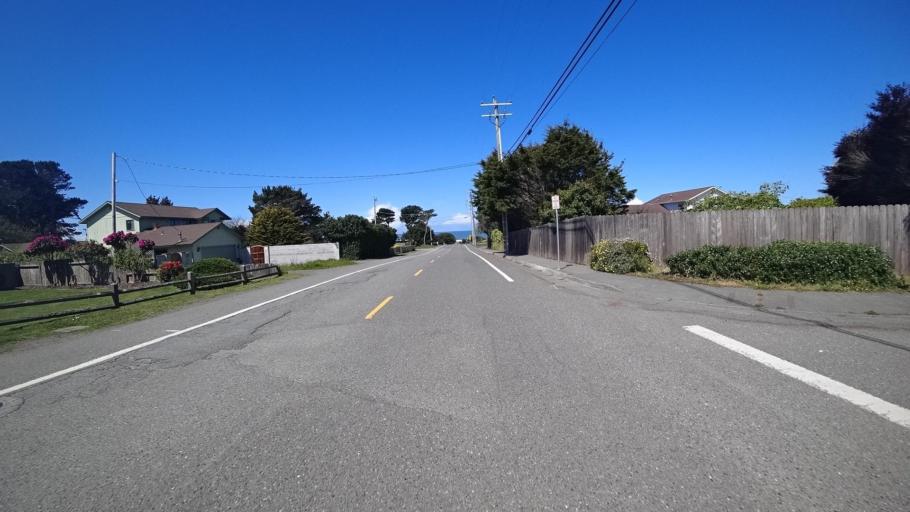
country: US
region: California
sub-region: Humboldt County
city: McKinleyville
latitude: 40.9562
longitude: -124.1192
